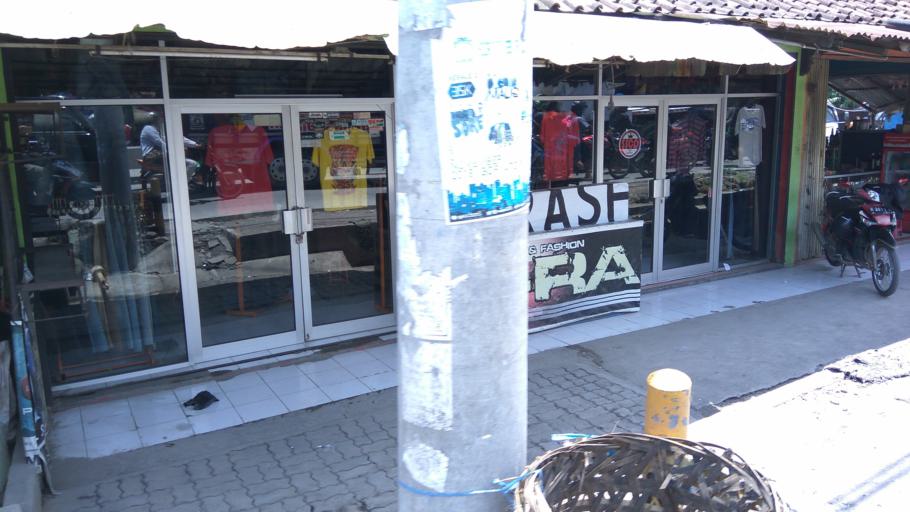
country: ID
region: Central Java
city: Mranggen
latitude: -7.0245
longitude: 110.5106
